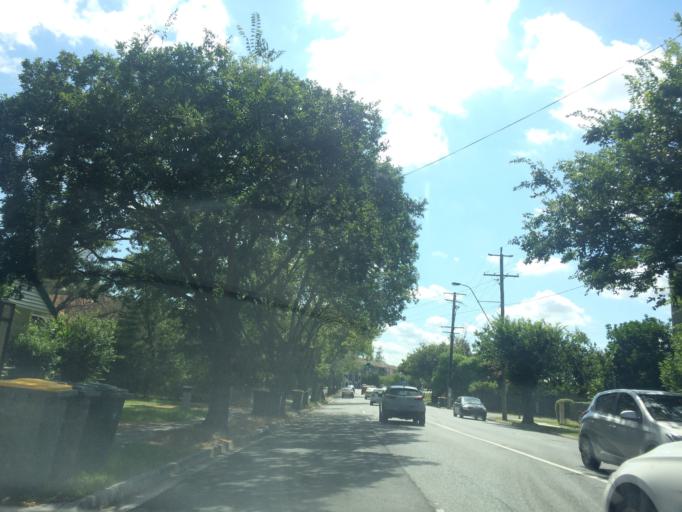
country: AU
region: Queensland
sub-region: Brisbane
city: Toowong
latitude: -27.4941
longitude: 153.0043
